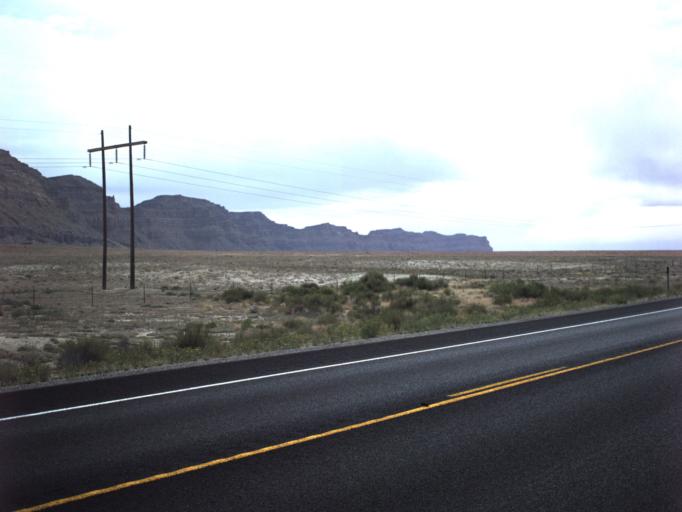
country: US
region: Utah
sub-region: Carbon County
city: East Carbon City
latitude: 39.1952
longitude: -110.3385
